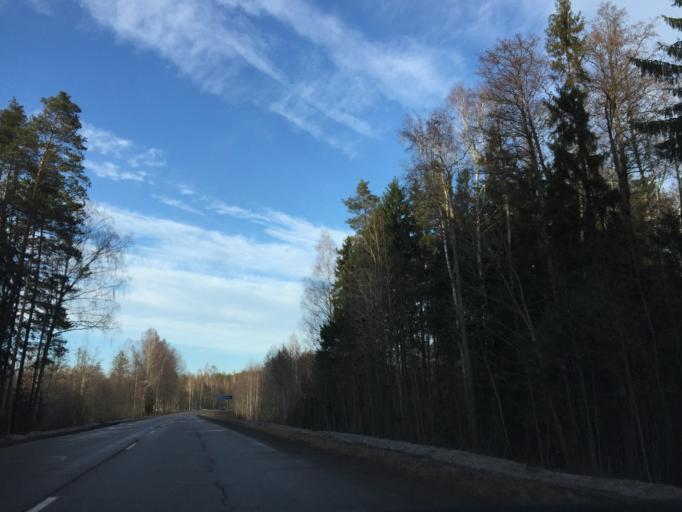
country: LV
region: Kekava
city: Balozi
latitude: 56.7484
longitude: 24.1074
